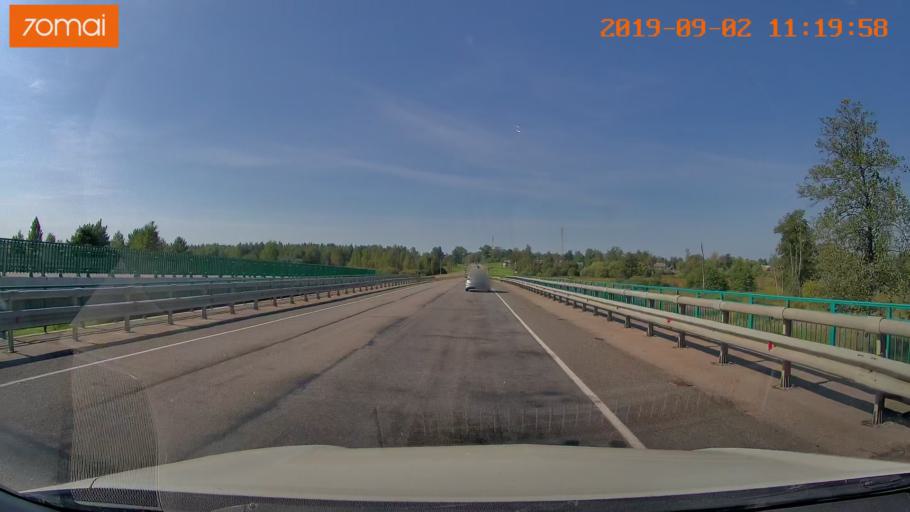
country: RU
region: Smolensk
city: Roslavl'
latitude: 54.0446
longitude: 33.0620
